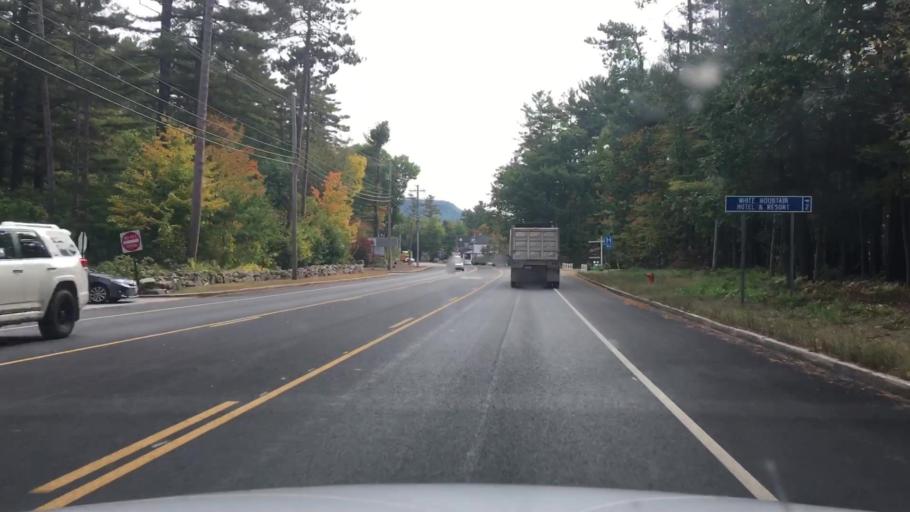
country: US
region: New Hampshire
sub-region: Carroll County
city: North Conway
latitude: 44.0607
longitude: -71.1387
